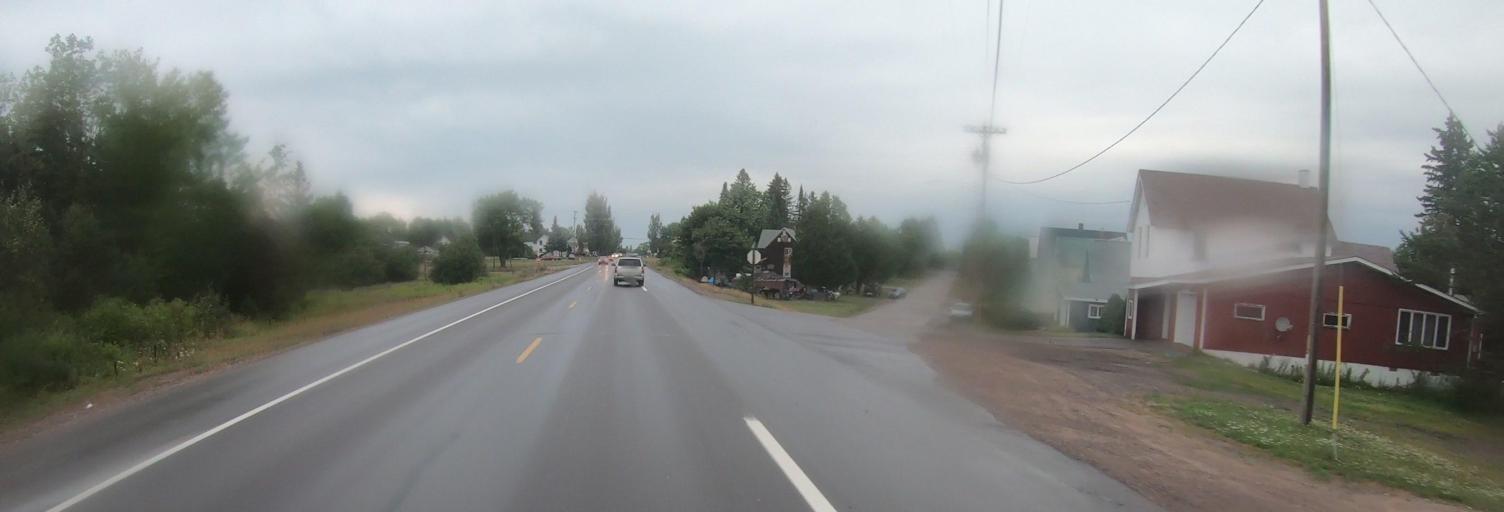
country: US
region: Michigan
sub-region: Houghton County
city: Laurium
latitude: 47.2294
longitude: -88.4540
